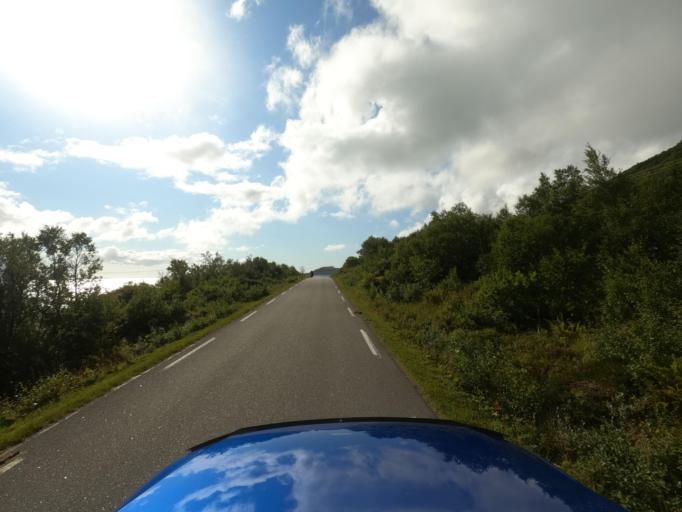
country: NO
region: Nordland
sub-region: Vagan
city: Kabelvag
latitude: 68.2506
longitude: 14.1530
